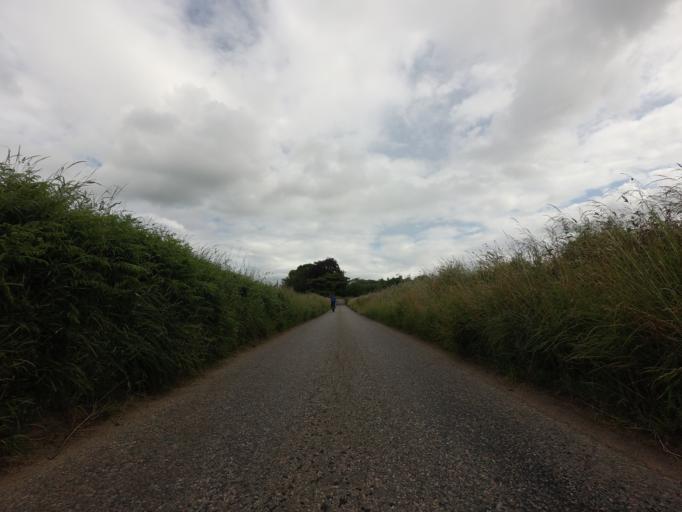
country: GB
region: Scotland
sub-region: Moray
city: Lhanbryd
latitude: 57.6505
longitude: -3.2395
